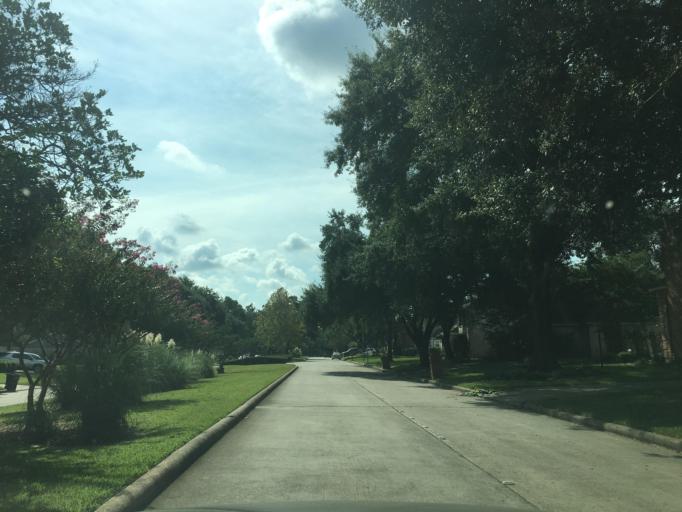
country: US
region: Texas
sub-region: Harris County
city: Spring
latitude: 30.0507
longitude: -95.4453
